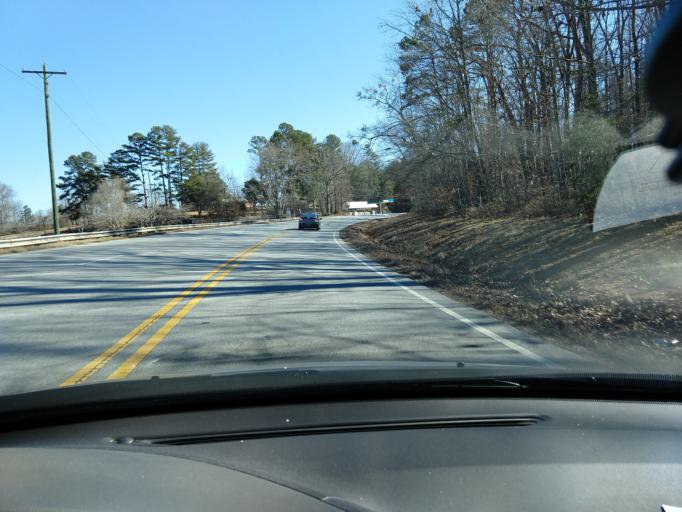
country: US
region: Georgia
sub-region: Stephens County
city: Toccoa
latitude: 34.6118
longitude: -83.3590
